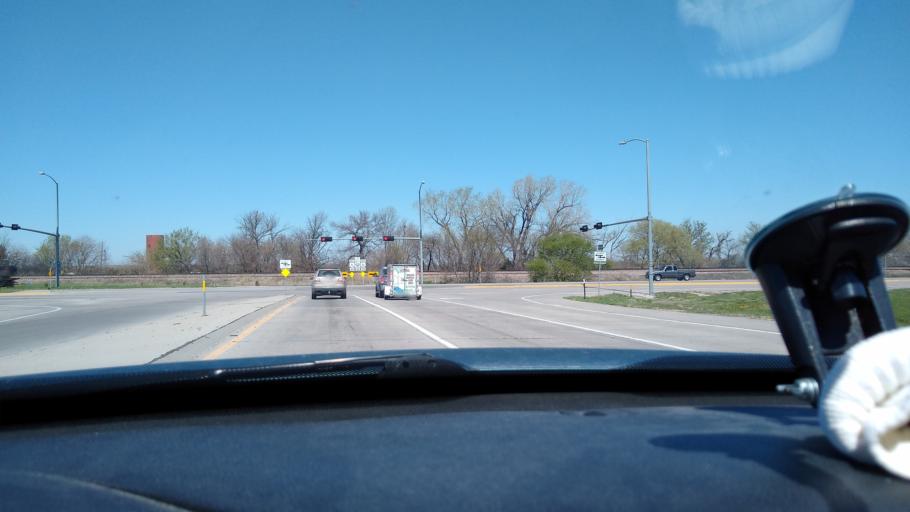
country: US
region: Nebraska
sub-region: Lancaster County
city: Waverly
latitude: 40.8968
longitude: -96.5641
